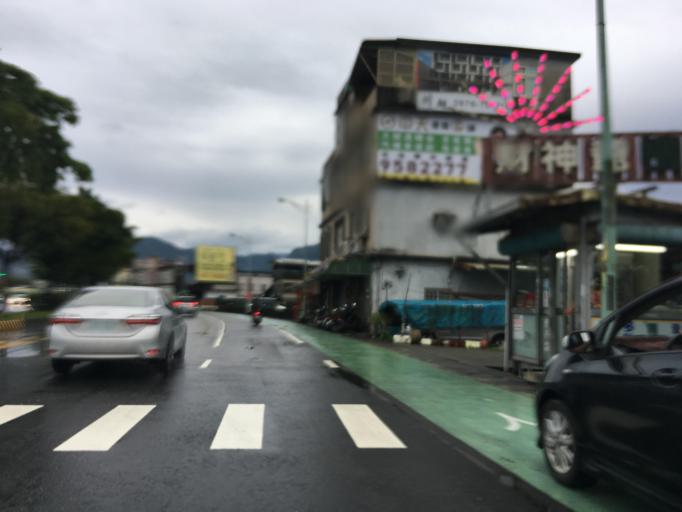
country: TW
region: Taiwan
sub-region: Yilan
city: Yilan
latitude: 24.6360
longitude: 121.7872
